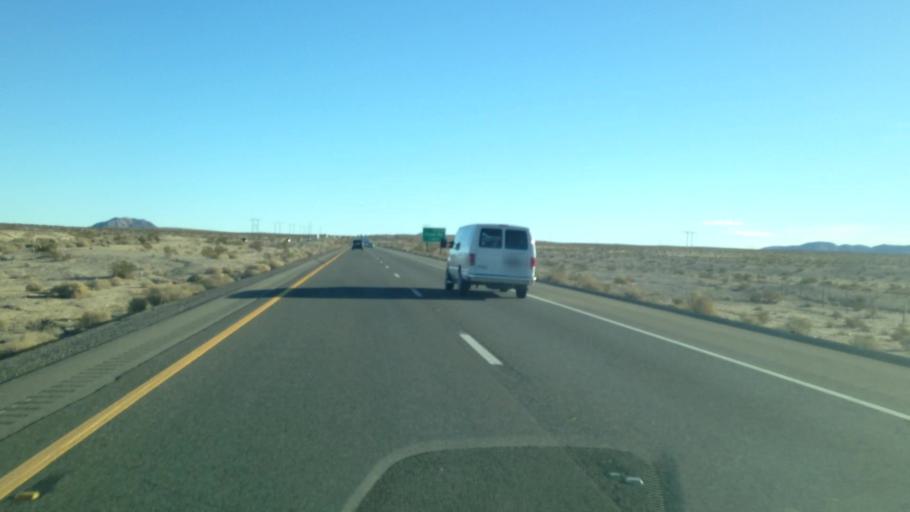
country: US
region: California
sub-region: San Bernardino County
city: Fort Irwin
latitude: 35.0028
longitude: -116.5538
